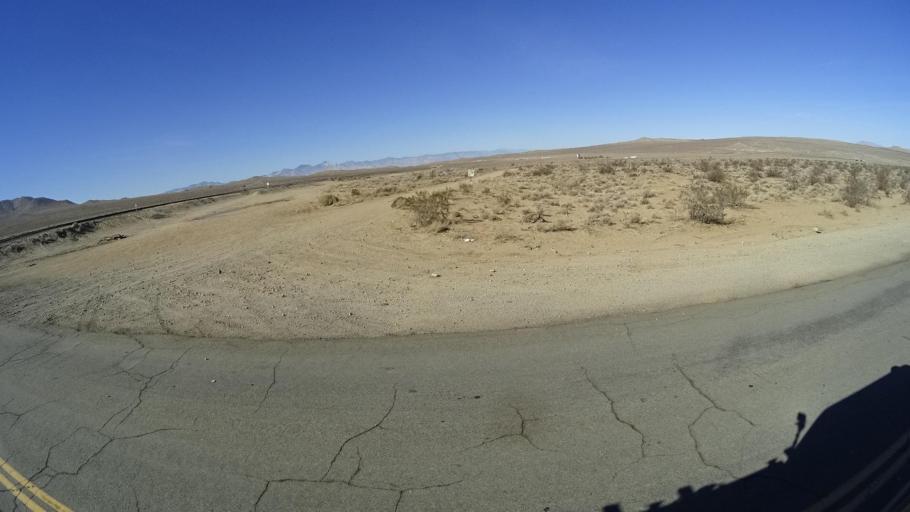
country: US
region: California
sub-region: Kern County
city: Ridgecrest
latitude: 35.4856
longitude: -117.6368
